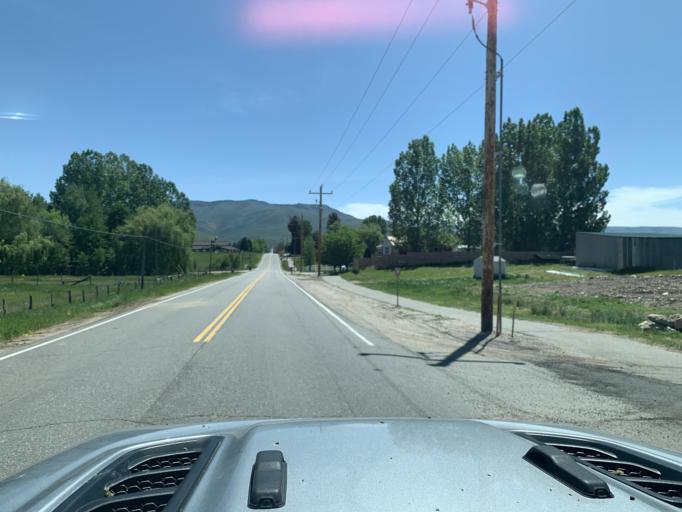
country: US
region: Utah
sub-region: Weber County
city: Wolf Creek
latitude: 41.2933
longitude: -111.7991
